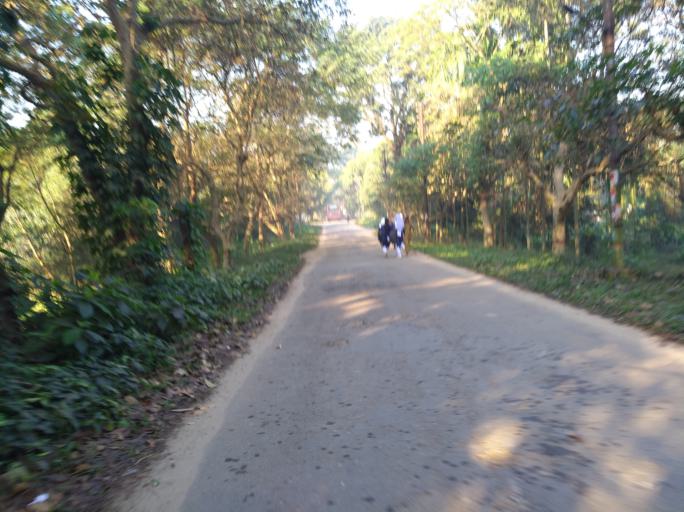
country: BD
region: Dhaka
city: Tungi
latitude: 23.8897
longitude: 90.2698
